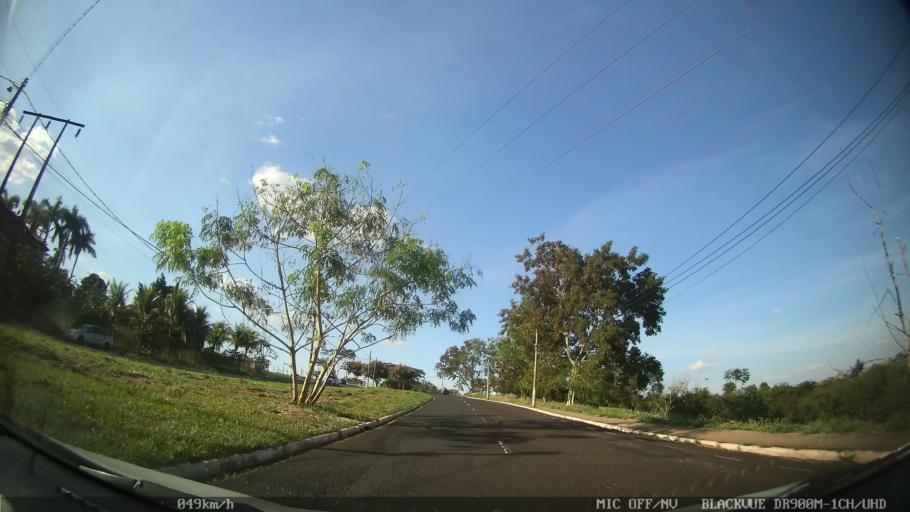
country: BR
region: Sao Paulo
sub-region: Ribeirao Preto
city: Ribeirao Preto
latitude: -21.2044
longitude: -47.7826
